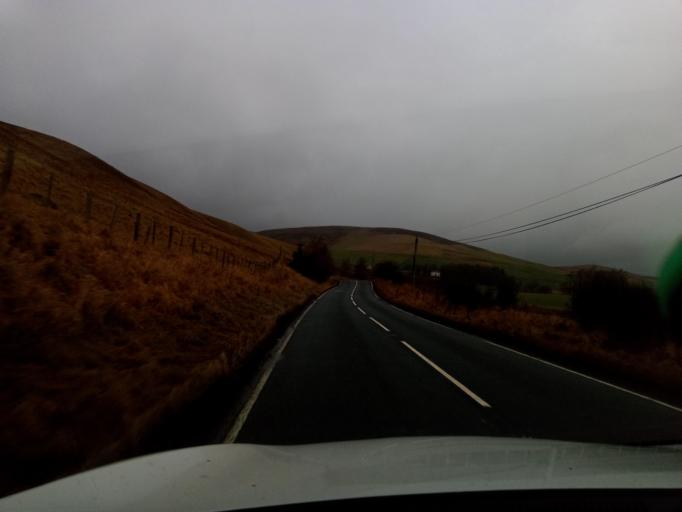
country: GB
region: Scotland
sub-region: The Scottish Borders
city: West Linton
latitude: 55.6586
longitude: -3.3081
